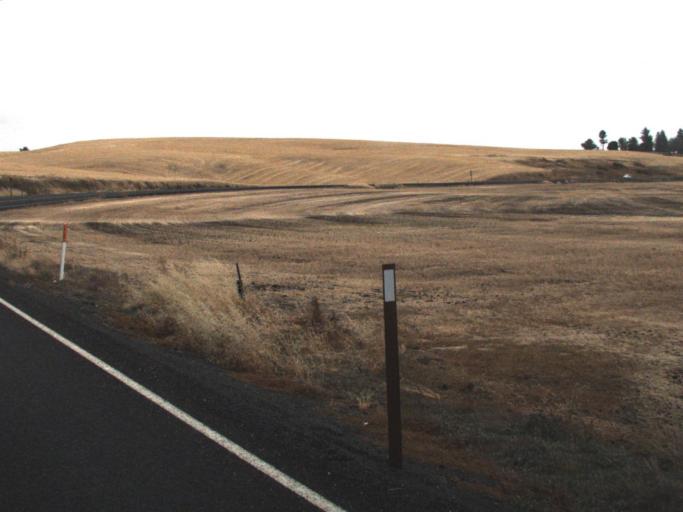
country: US
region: Washington
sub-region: Whitman County
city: Colfax
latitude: 47.1451
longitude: -117.2539
